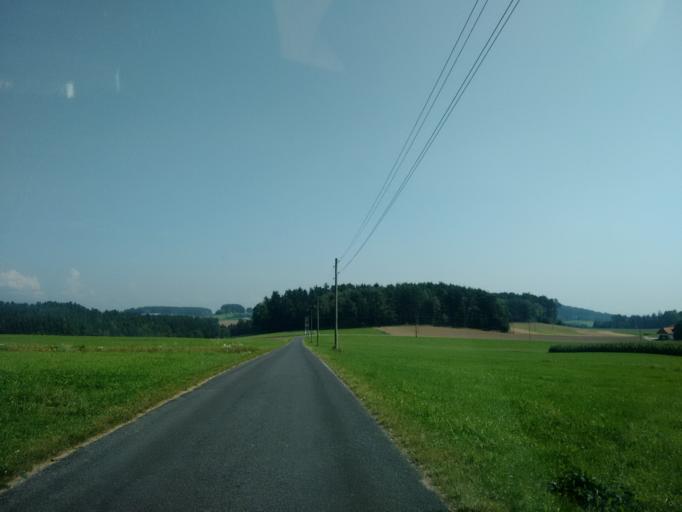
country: AT
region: Upper Austria
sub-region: Politischer Bezirk Urfahr-Umgebung
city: Haibach im Muhlkreis
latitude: 48.4111
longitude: 14.3531
